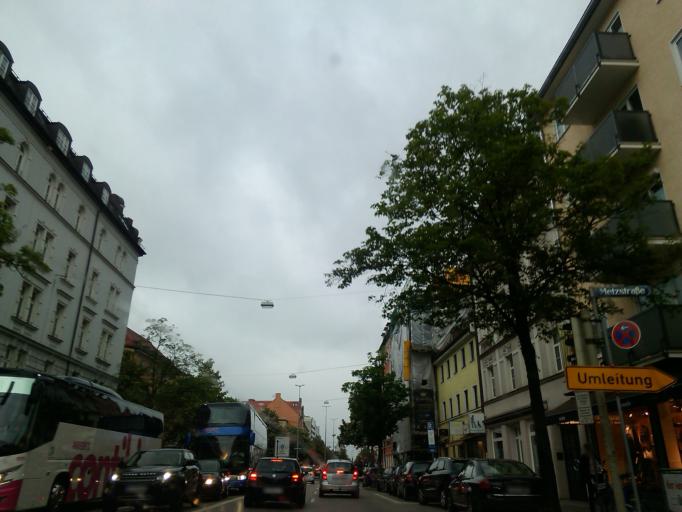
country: DE
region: Bavaria
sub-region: Upper Bavaria
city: Munich
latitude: 48.1279
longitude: 11.5952
